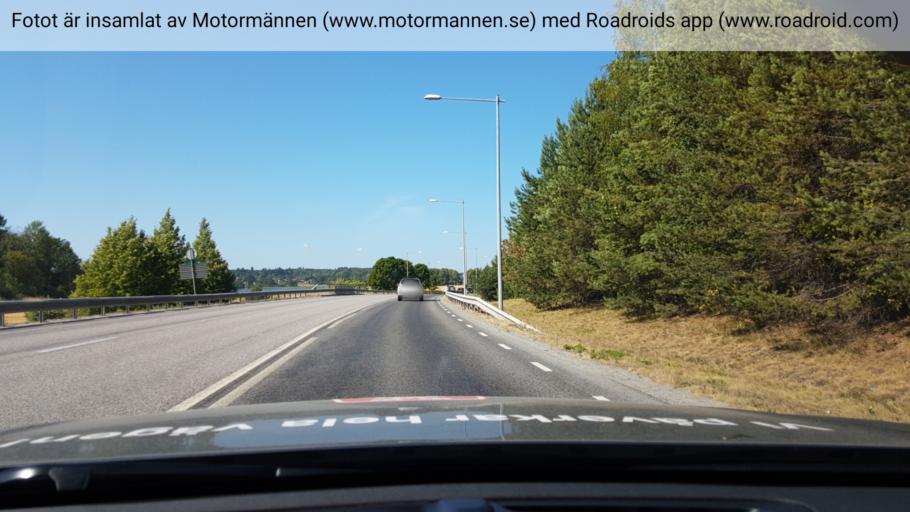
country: SE
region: Stockholm
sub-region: Ekero Kommun
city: Ekeroe
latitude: 59.2972
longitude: 17.8486
